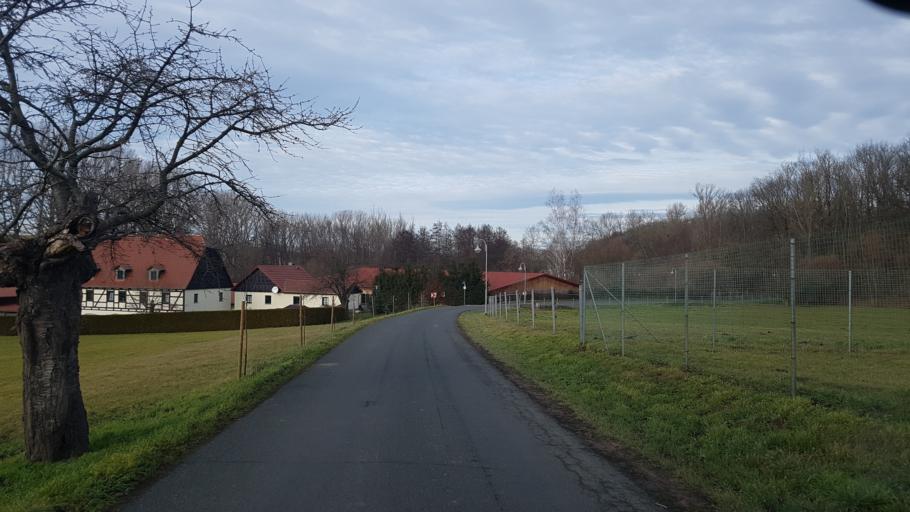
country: DE
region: Saxony
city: Ostrau
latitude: 51.1858
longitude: 13.1710
